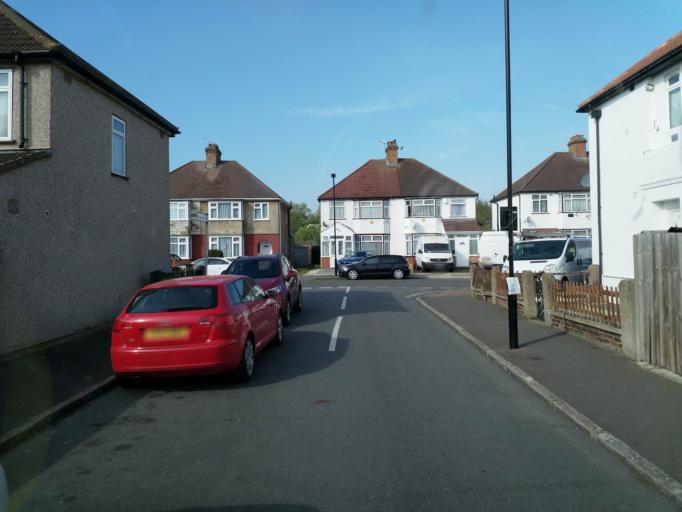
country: GB
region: England
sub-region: Greater London
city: Hounslow
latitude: 51.4628
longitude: -0.3846
